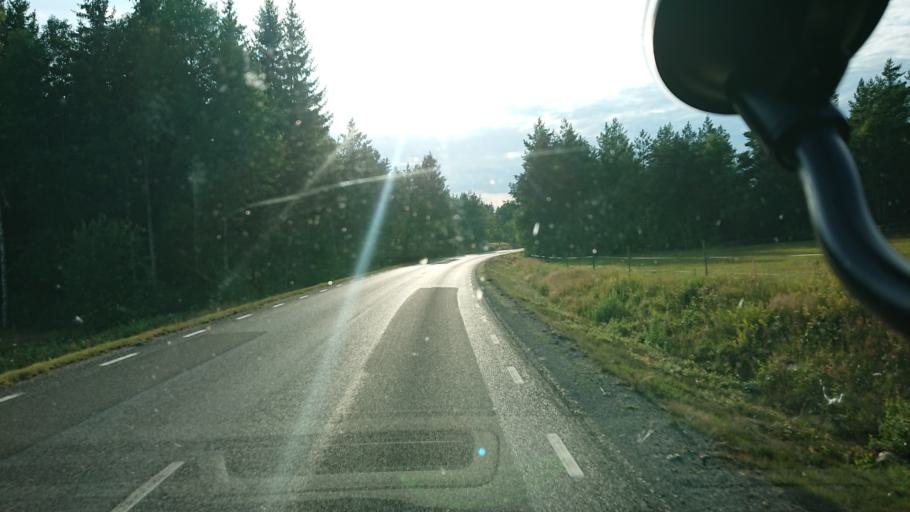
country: SE
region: Kronoberg
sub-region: Vaxjo Kommun
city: Rottne
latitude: 57.0333
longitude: 14.9506
